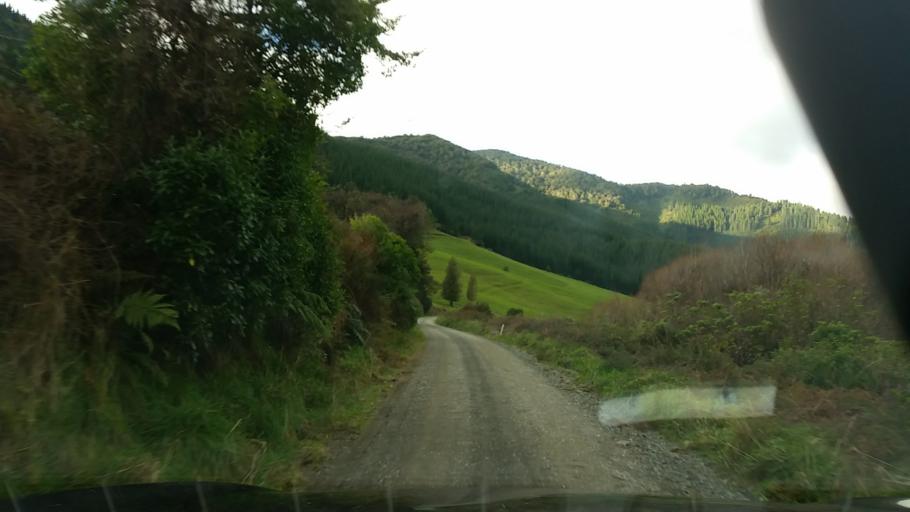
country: NZ
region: Nelson
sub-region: Nelson City
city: Nelson
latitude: -41.2099
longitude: 173.6320
